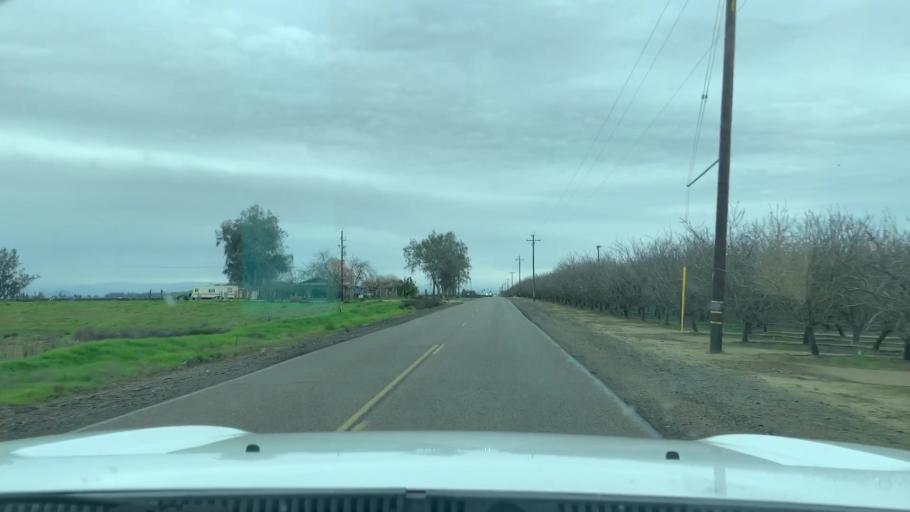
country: US
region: California
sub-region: Fresno County
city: Caruthers
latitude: 36.5473
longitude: -119.7541
